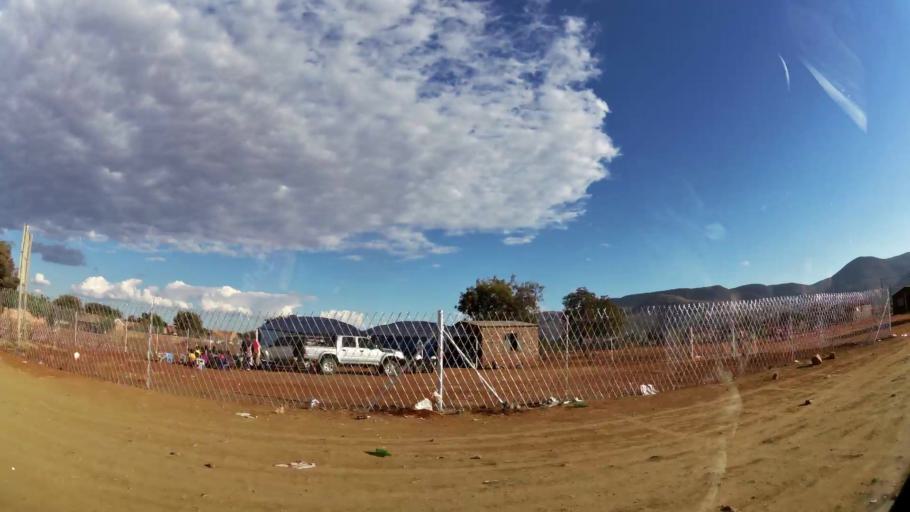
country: ZA
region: Limpopo
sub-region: Waterberg District Municipality
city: Mokopane
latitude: -24.1947
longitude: 28.9883
